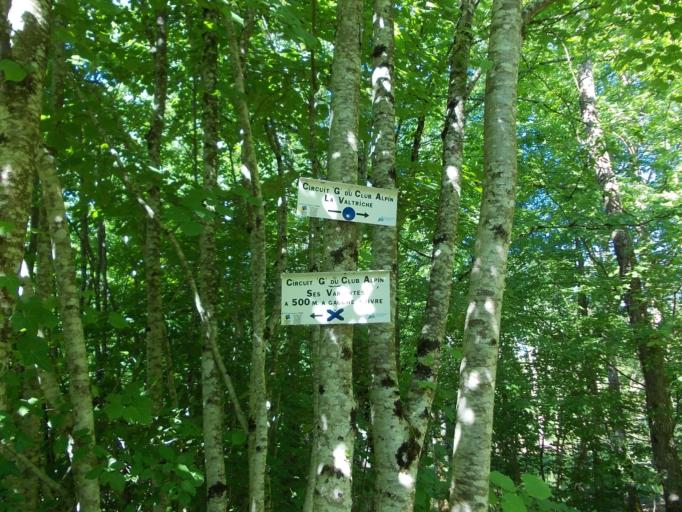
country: FR
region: Lorraine
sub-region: Departement de Meurthe-et-Moselle
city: Pompey
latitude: 48.7442
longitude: 6.1025
